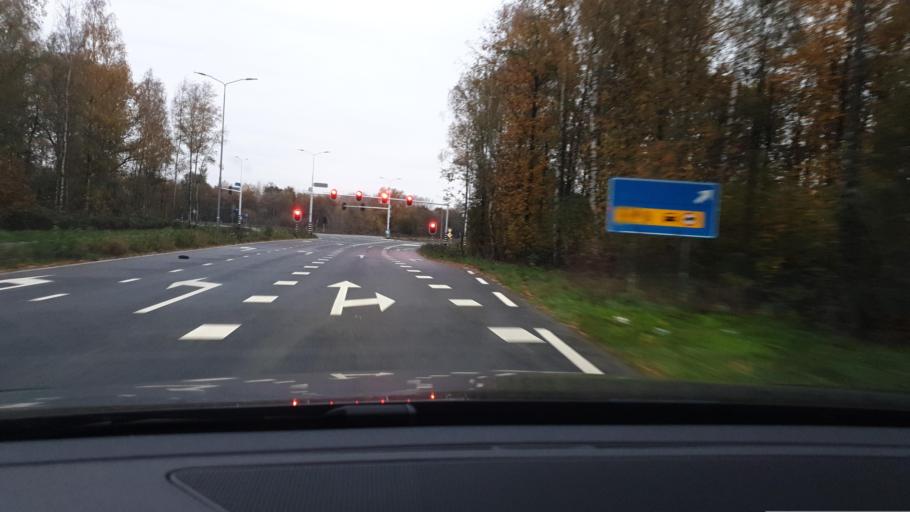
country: NL
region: North Brabant
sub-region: Gemeente Best
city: Best
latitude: 51.4780
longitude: 5.3872
